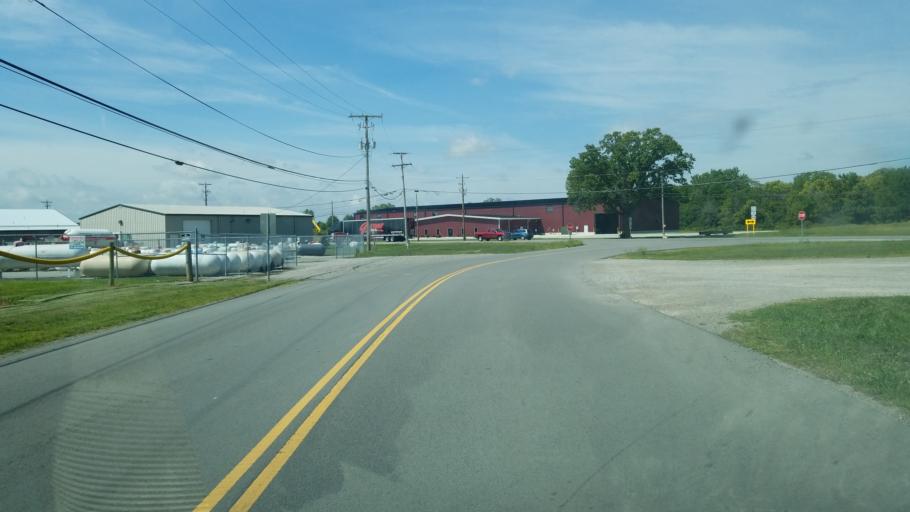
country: US
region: Ohio
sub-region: Hardin County
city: Kenton
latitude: 40.6325
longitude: -83.6140
